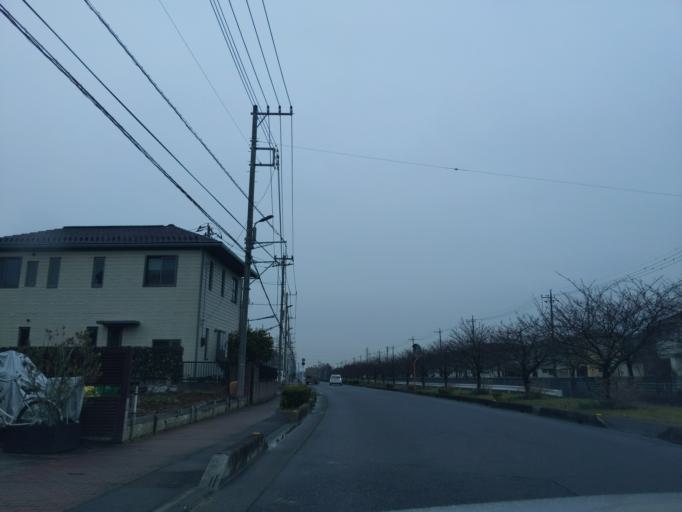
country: JP
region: Saitama
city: Koshigaya
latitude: 35.8563
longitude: 139.7667
